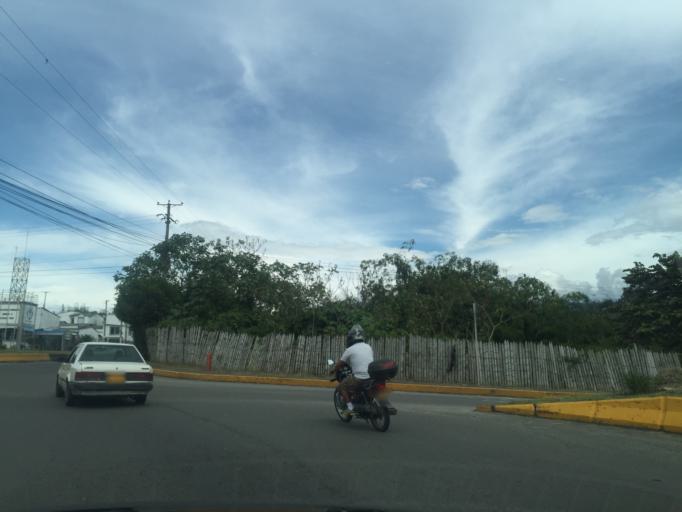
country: CO
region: Quindio
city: Armenia
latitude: 4.5308
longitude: -75.7009
